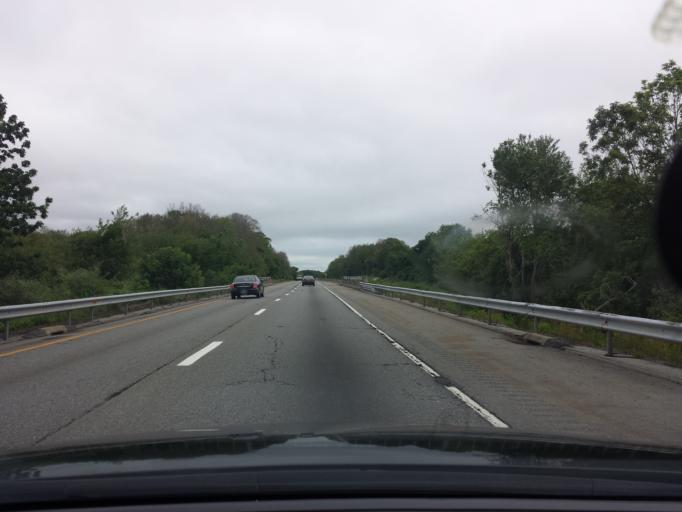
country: US
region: Connecticut
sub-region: New London County
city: Old Mystic
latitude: 41.3783
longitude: -71.9053
